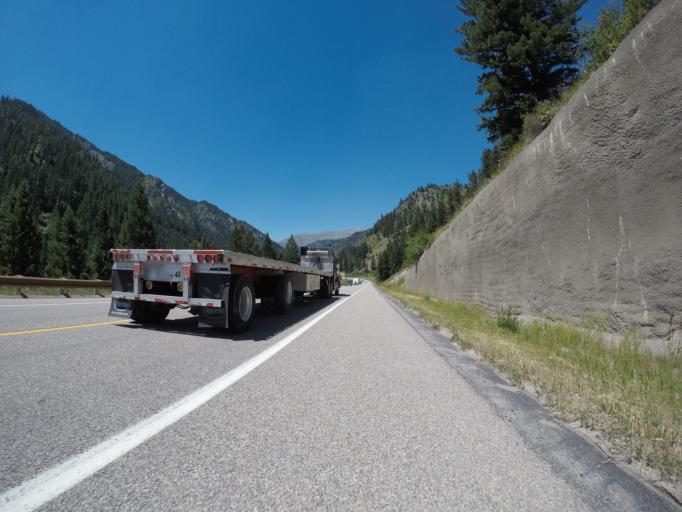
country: US
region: Wyoming
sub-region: Teton County
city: Hoback
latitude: 43.1963
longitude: -110.8793
